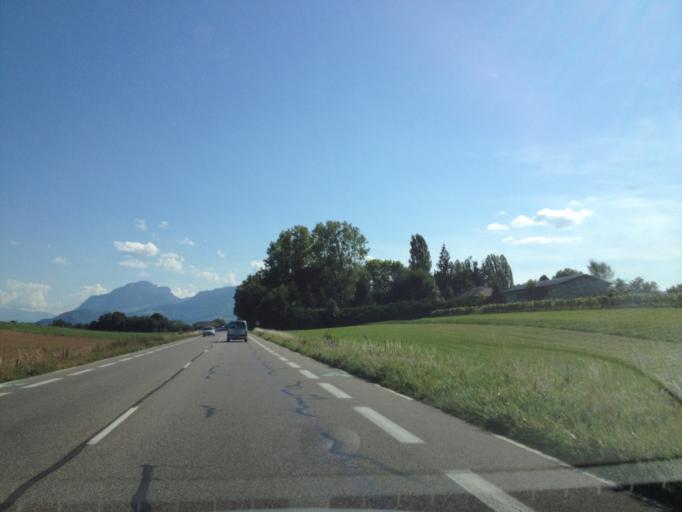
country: FR
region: Rhone-Alpes
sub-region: Departement de la Savoie
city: Sonnaz
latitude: 45.6206
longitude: 5.9111
